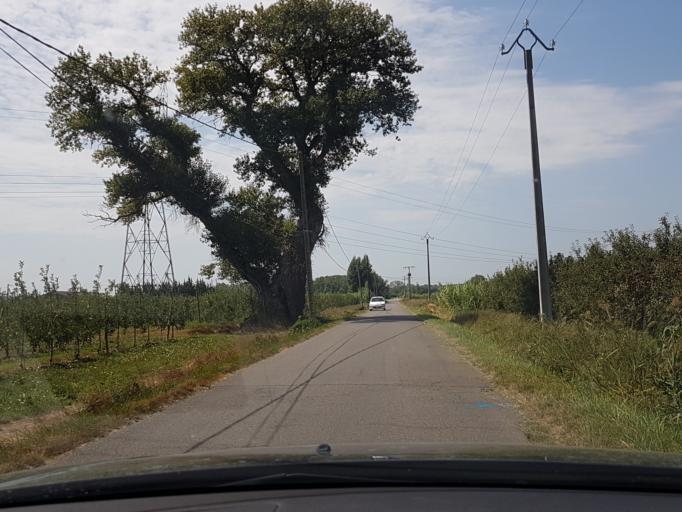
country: FR
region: Provence-Alpes-Cote d'Azur
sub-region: Departement des Bouches-du-Rhone
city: Molleges
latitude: 43.8052
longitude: 4.8921
